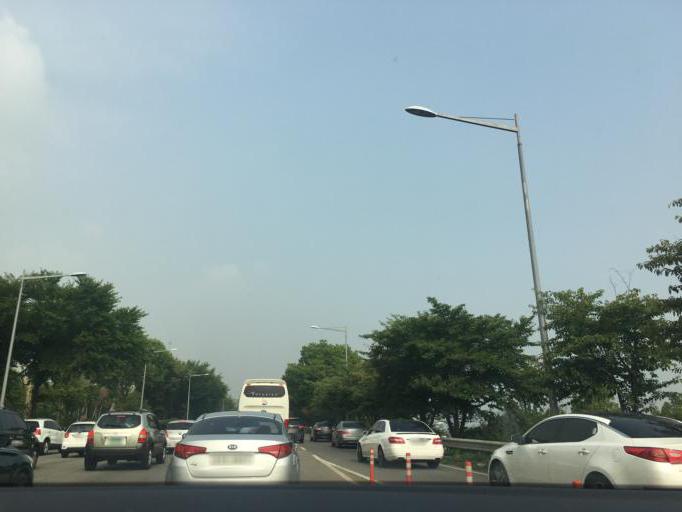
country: KR
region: Gyeonggi-do
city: Seongnam-si
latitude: 37.5178
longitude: 127.0758
